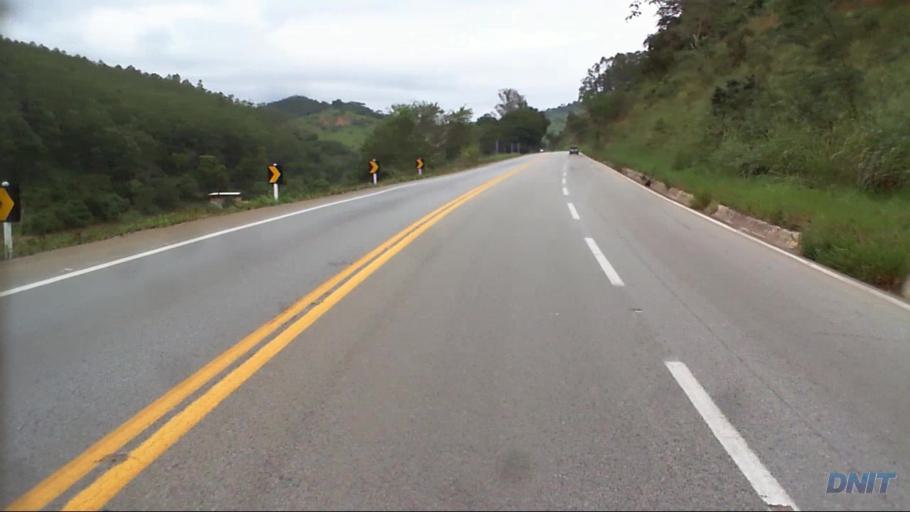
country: BR
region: Minas Gerais
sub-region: Nova Era
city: Nova Era
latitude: -19.7777
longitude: -43.0438
